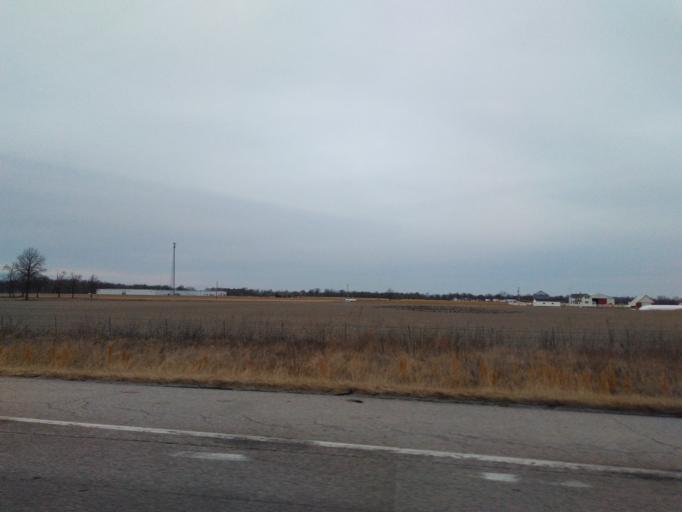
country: US
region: Illinois
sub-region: Washington County
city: Nashville
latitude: 38.3913
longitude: -89.3647
